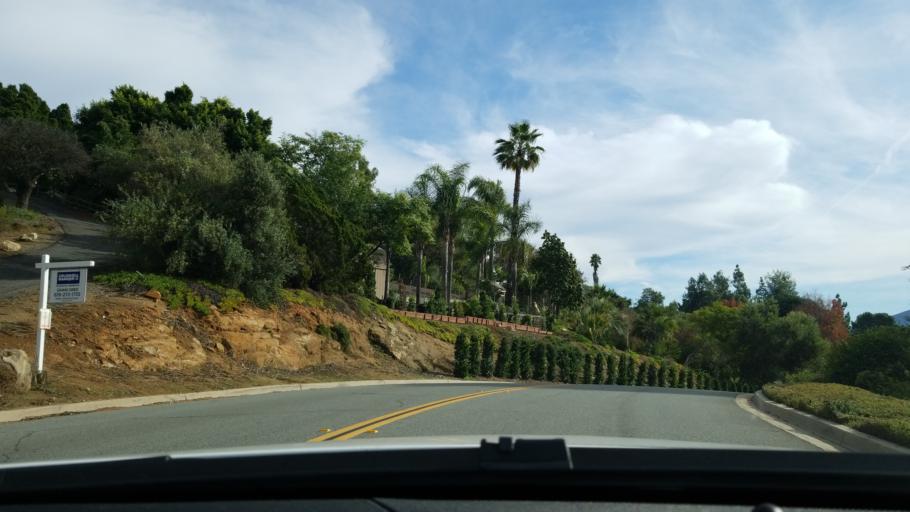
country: US
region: California
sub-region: San Diego County
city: Casa de Oro-Mount Helix
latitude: 32.7689
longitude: -116.9532
